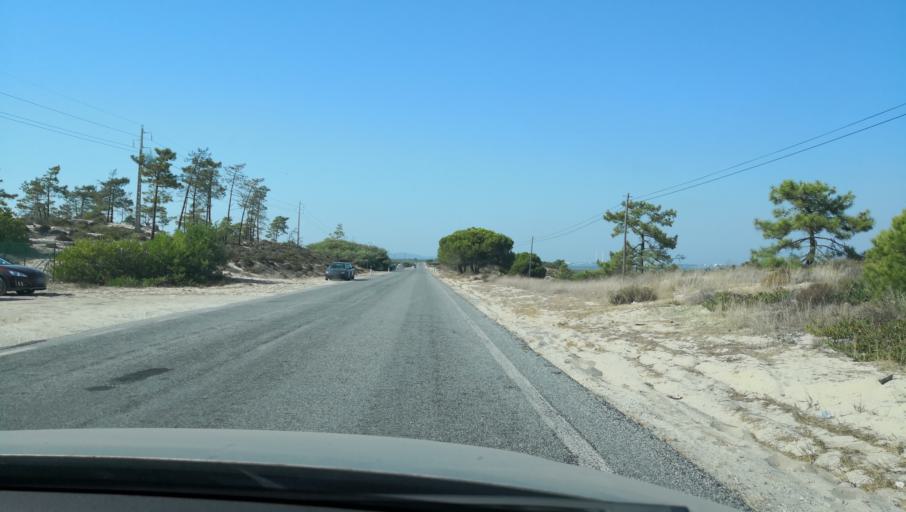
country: PT
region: Setubal
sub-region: Setubal
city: Setubal
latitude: 38.4216
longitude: -8.8214
